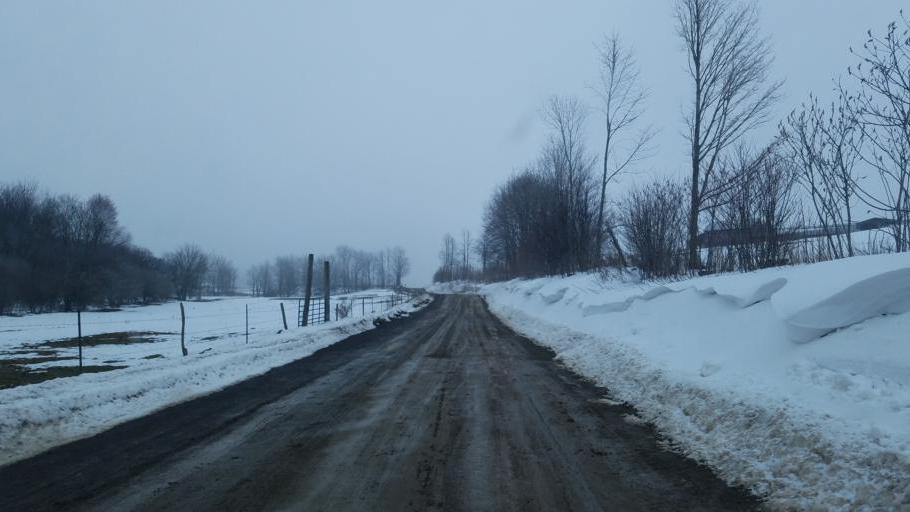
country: US
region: New York
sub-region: Allegany County
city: Andover
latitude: 41.9443
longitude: -77.7687
